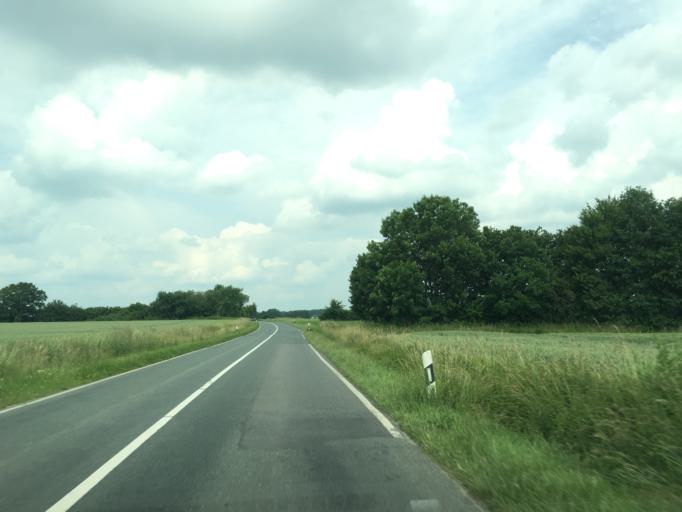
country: DE
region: North Rhine-Westphalia
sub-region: Regierungsbezirk Munster
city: Laer
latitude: 52.0454
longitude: 7.3739
